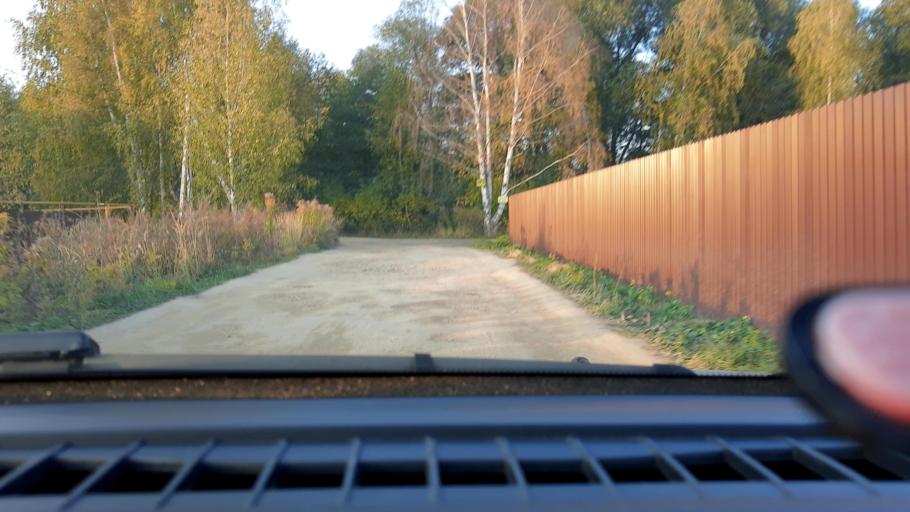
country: RU
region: Nizjnij Novgorod
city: Bor
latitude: 56.4019
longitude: 44.0367
